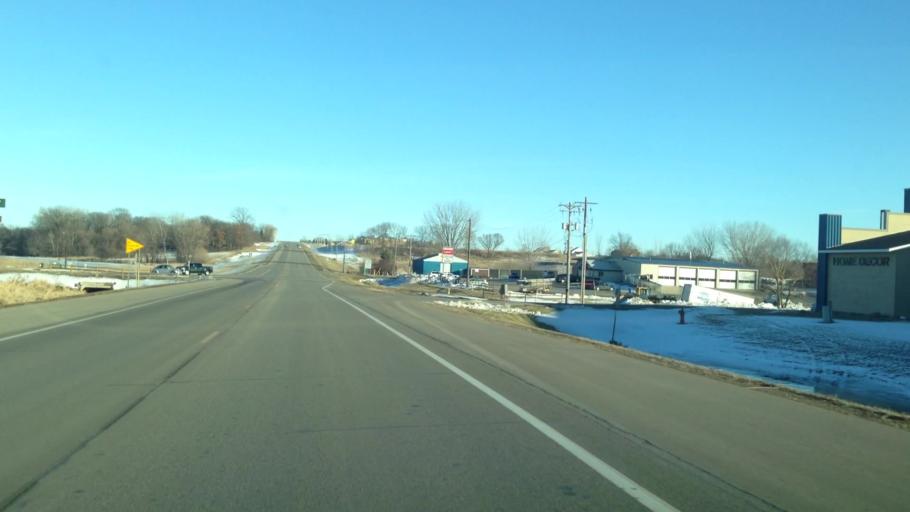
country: US
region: Minnesota
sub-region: Rice County
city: Lonsdale
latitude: 44.4791
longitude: -93.4190
